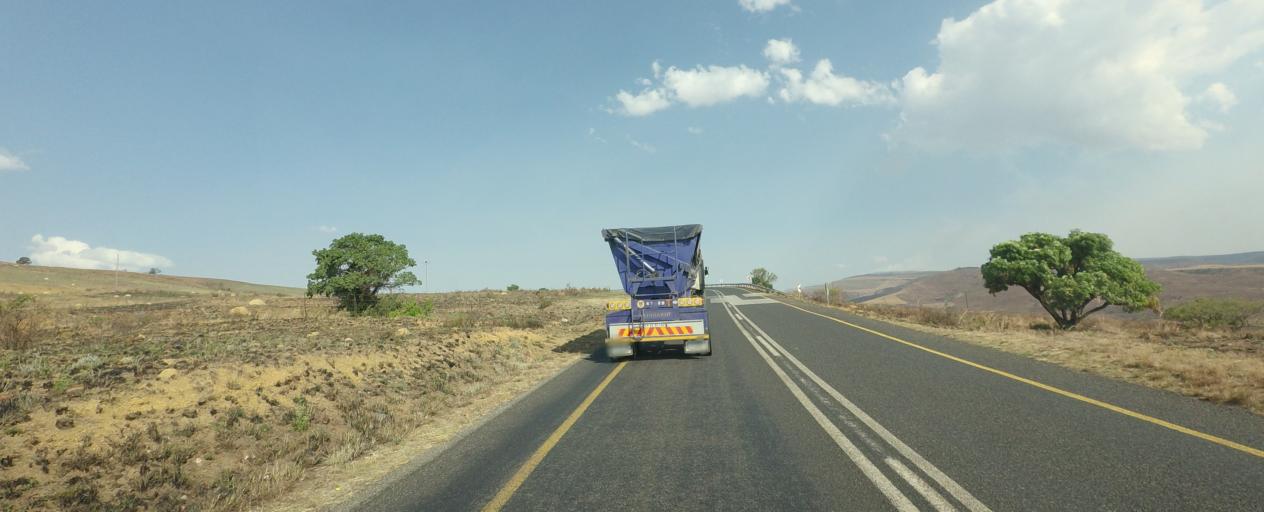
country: ZA
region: Mpumalanga
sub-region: Ehlanzeni District
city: Lydenburg
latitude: -25.1106
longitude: 30.4983
